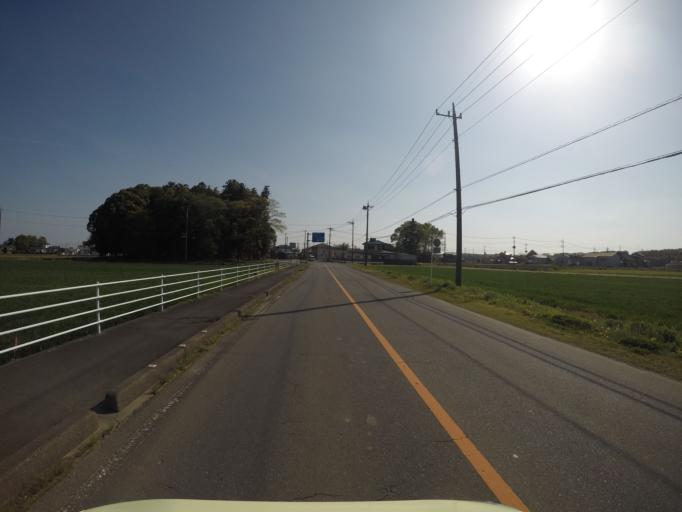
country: JP
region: Ibaraki
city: Yuki
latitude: 36.3388
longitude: 139.8920
